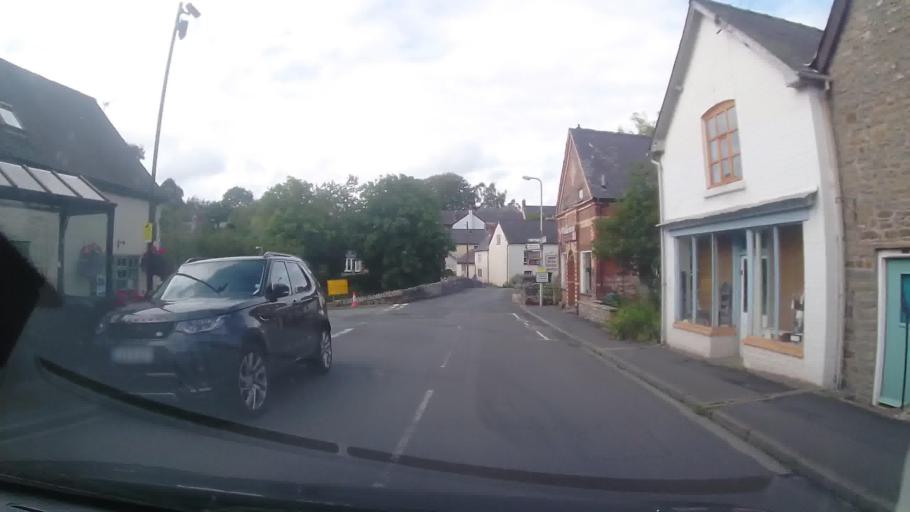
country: GB
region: England
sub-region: Shropshire
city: Acton
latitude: 52.4200
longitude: -3.0302
